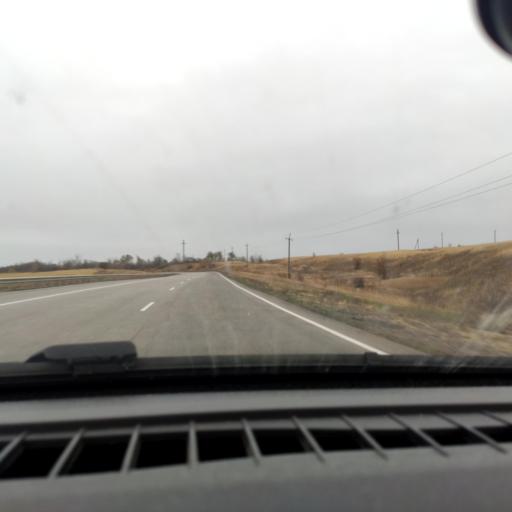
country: RU
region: Voronezj
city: Uryv-Pokrovka
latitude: 51.1360
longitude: 39.0494
